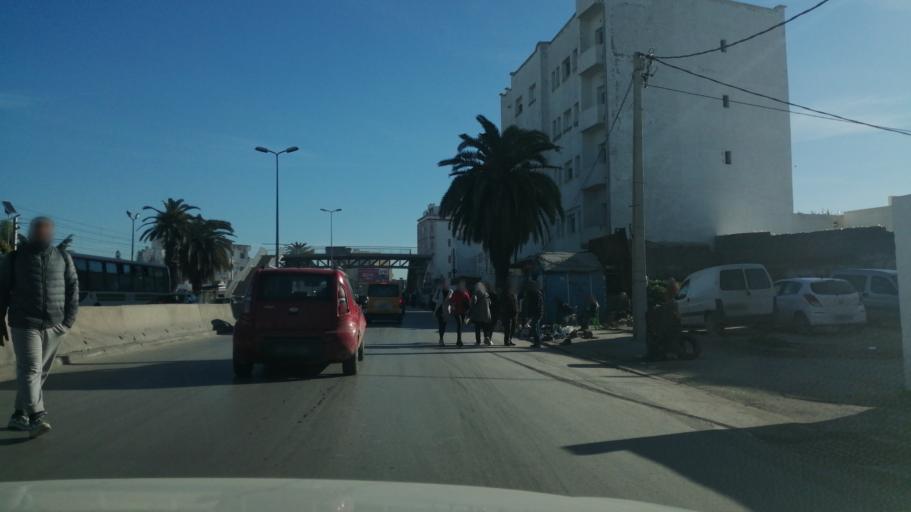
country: TN
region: Tunis
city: Tunis
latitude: 36.8096
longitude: 10.1621
